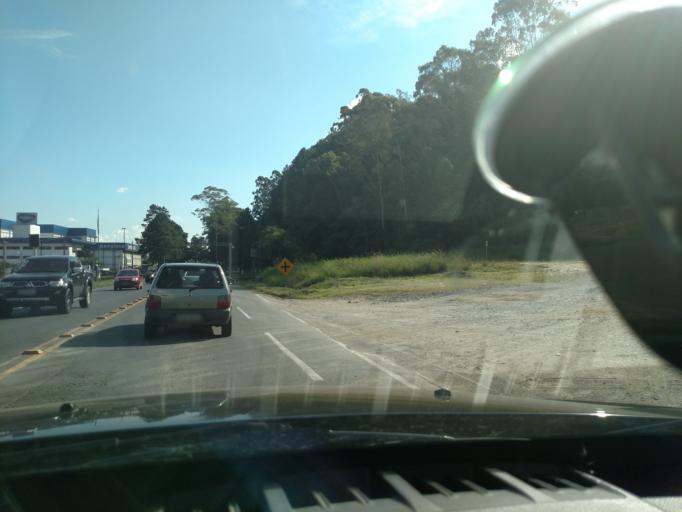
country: BR
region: Santa Catarina
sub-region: Rio Do Sul
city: Rio do Sul
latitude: -27.2386
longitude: -49.6837
